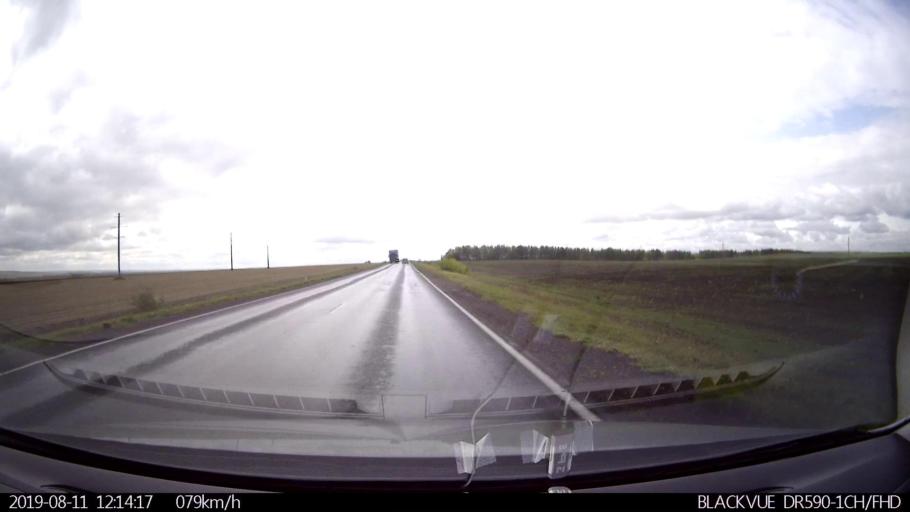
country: RU
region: Ulyanovsk
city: Ignatovka
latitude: 53.9537
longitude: 47.9821
